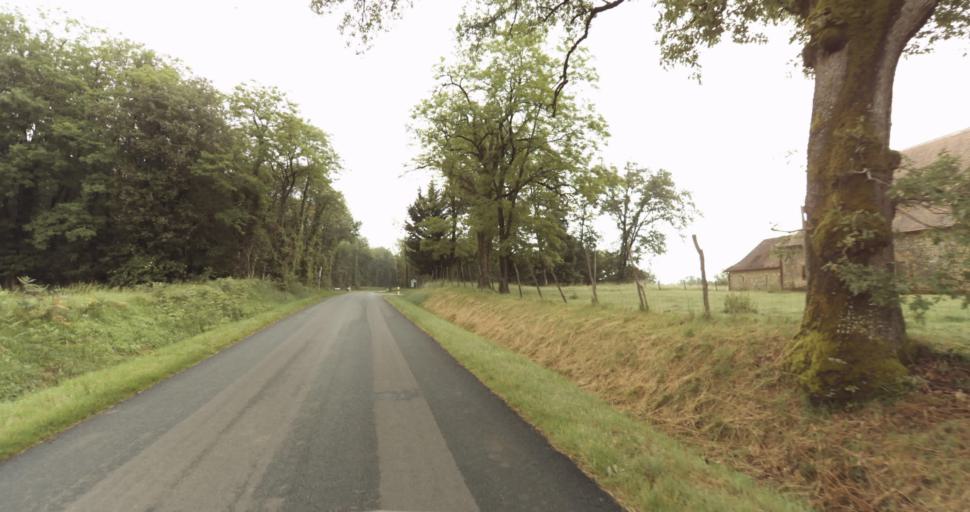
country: FR
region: Aquitaine
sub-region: Departement de la Dordogne
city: Lalinde
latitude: 44.9040
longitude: 0.7774
